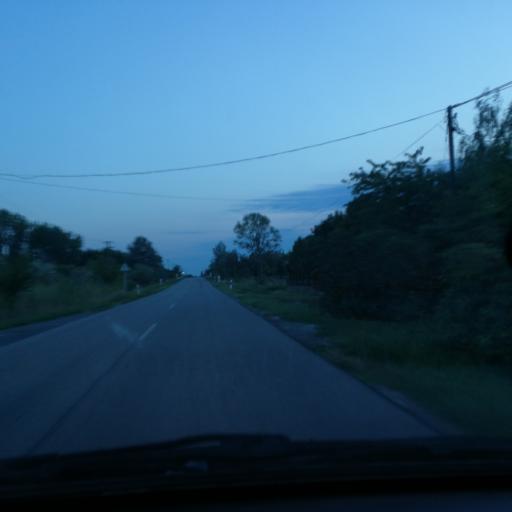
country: HU
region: Bacs-Kiskun
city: Csaszartoltes
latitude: 46.5247
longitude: 19.1212
